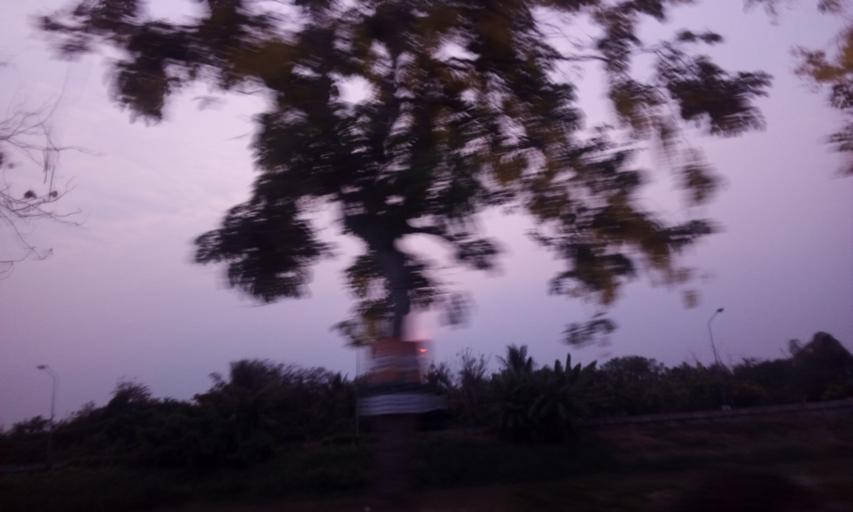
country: TH
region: Pathum Thani
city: Nong Suea
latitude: 14.0448
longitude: 100.8934
